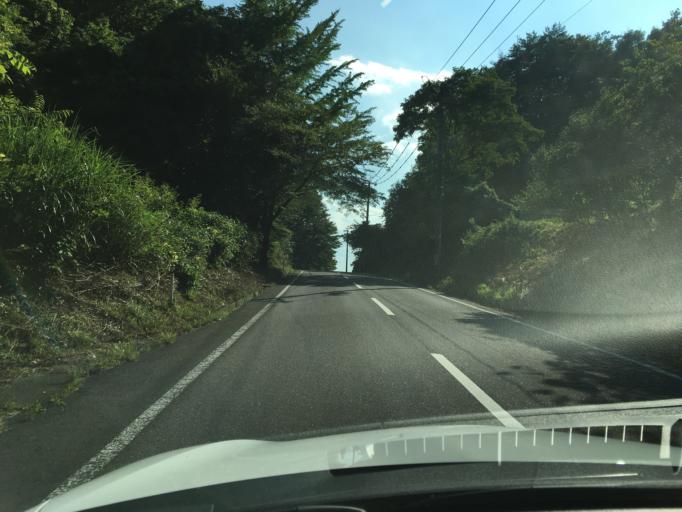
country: JP
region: Fukushima
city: Ishikawa
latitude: 37.2006
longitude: 140.5043
